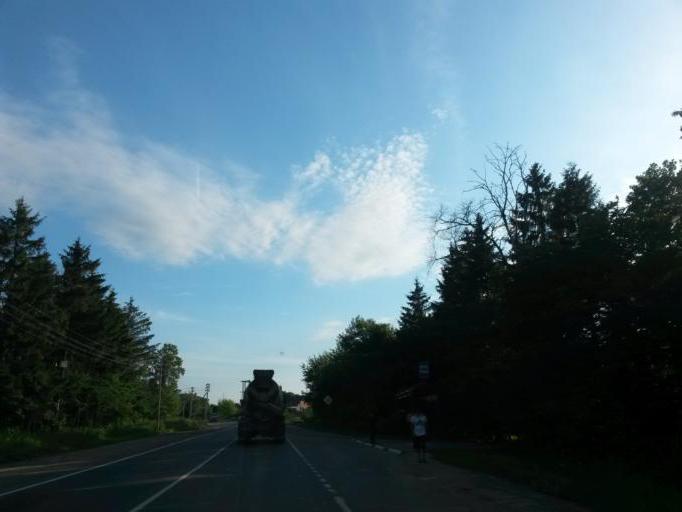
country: RU
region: Moskovskaya
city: Yam
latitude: 55.4675
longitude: 37.7040
